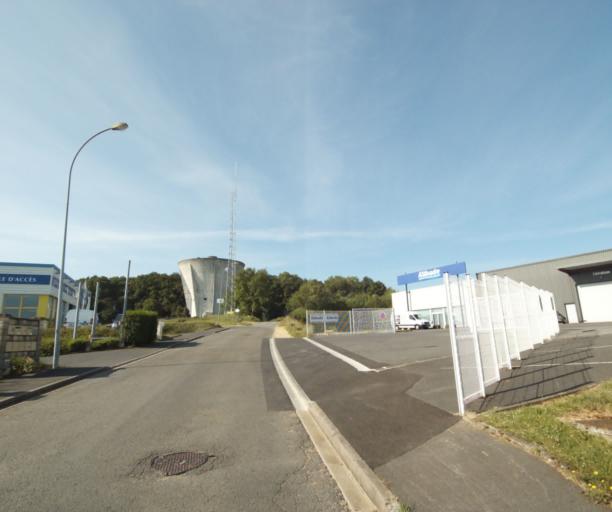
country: FR
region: Champagne-Ardenne
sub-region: Departement des Ardennes
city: La Francheville
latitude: 49.7375
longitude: 4.7046
